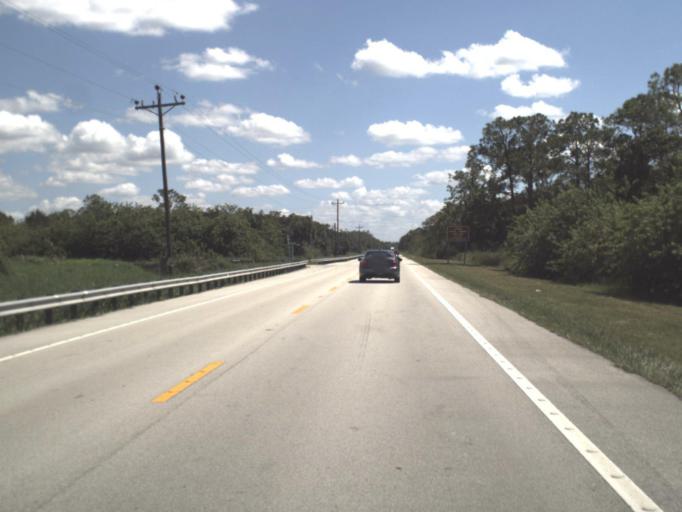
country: US
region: Florida
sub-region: Collier County
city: Lely Resort
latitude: 26.0064
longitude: -81.6104
